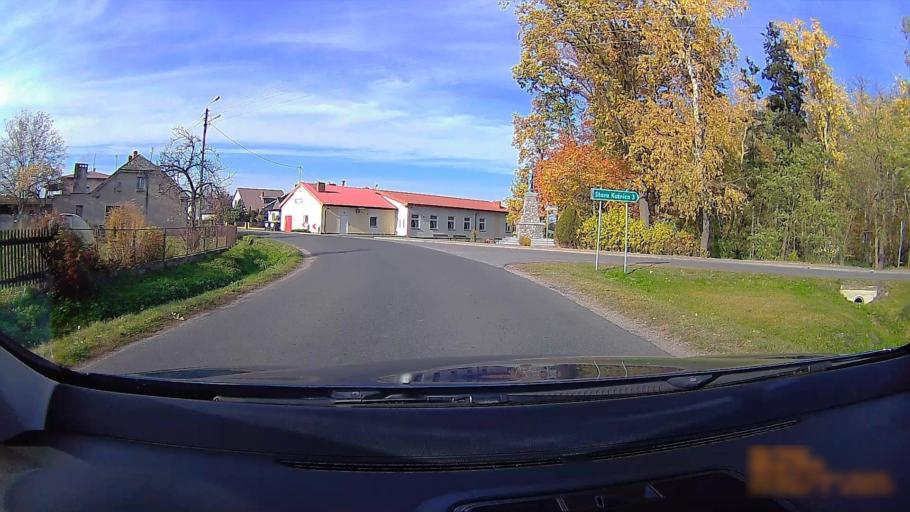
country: PL
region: Greater Poland Voivodeship
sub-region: Powiat ostrzeszowski
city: Doruchow
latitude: 51.4277
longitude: 18.0512
